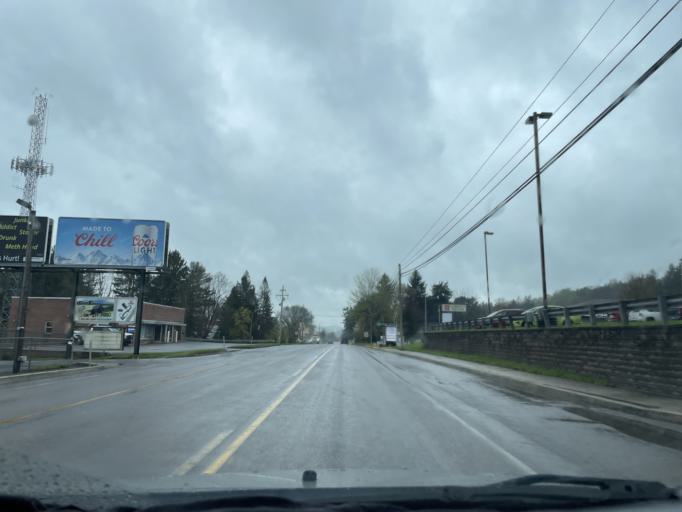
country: US
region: Maryland
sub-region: Garrett County
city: Oakland
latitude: 39.4190
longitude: -79.4003
